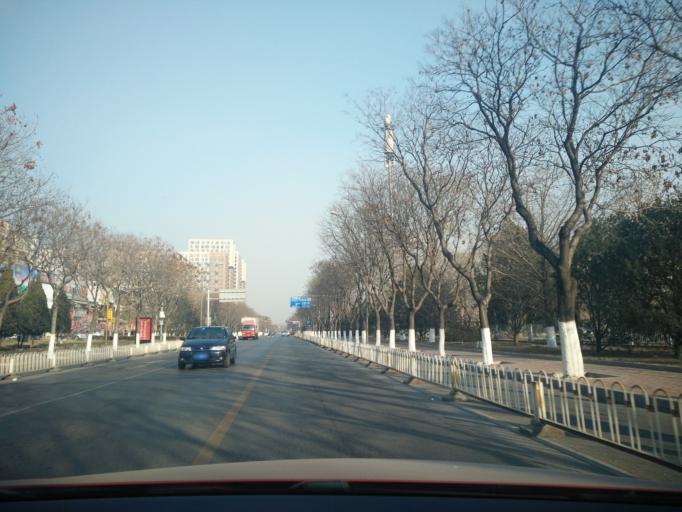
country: CN
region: Beijing
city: Jiugong
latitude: 39.8067
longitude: 116.4986
